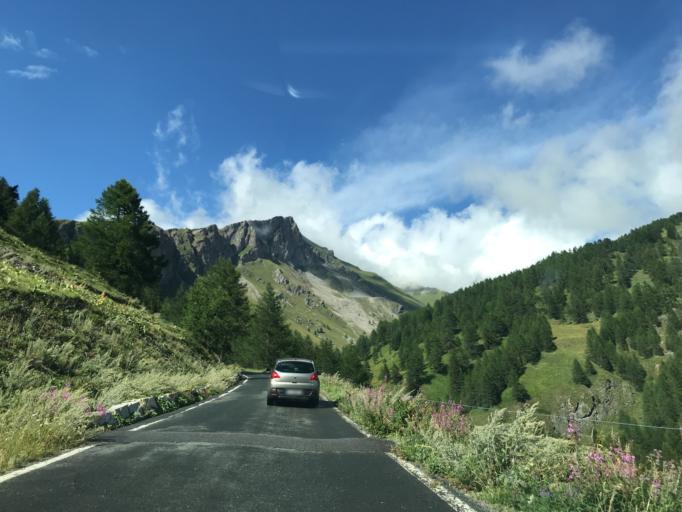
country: IT
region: Piedmont
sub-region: Provincia di Cuneo
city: Pontechianale
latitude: 44.6539
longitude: 6.9887
